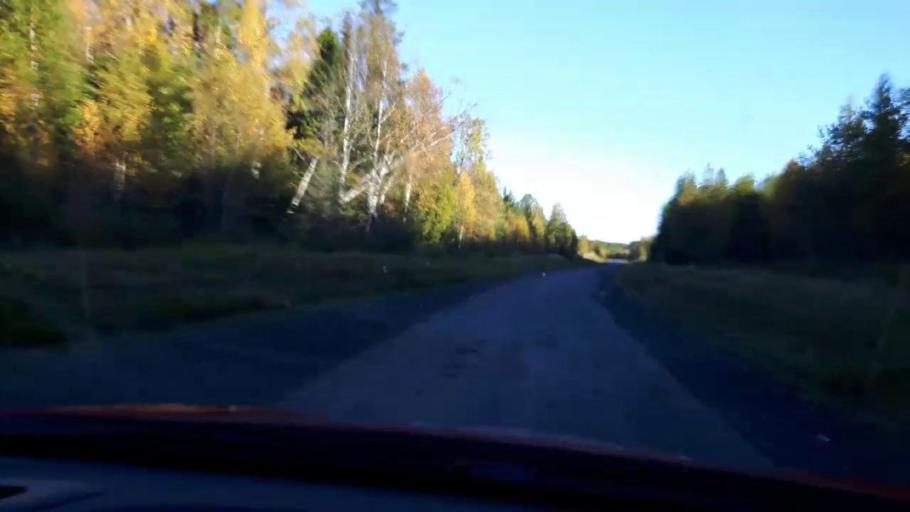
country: SE
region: Jaemtland
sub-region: OEstersunds Kommun
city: Lit
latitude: 63.5940
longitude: 14.8360
